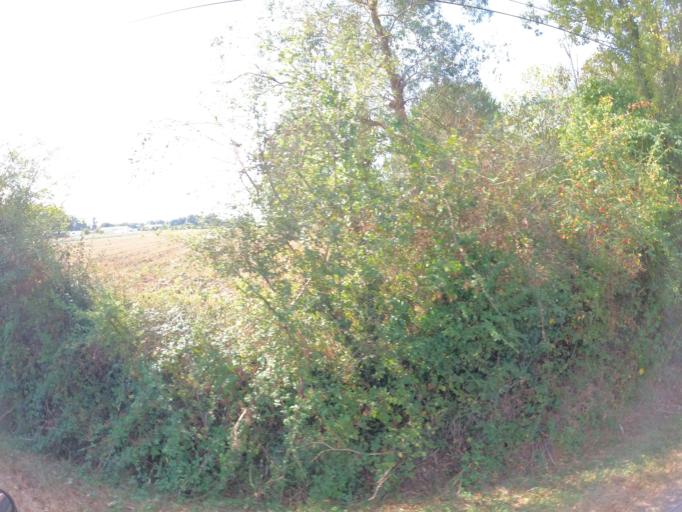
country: FR
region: Pays de la Loire
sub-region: Departement de la Vendee
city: Challans
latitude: 46.8094
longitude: -1.8405
